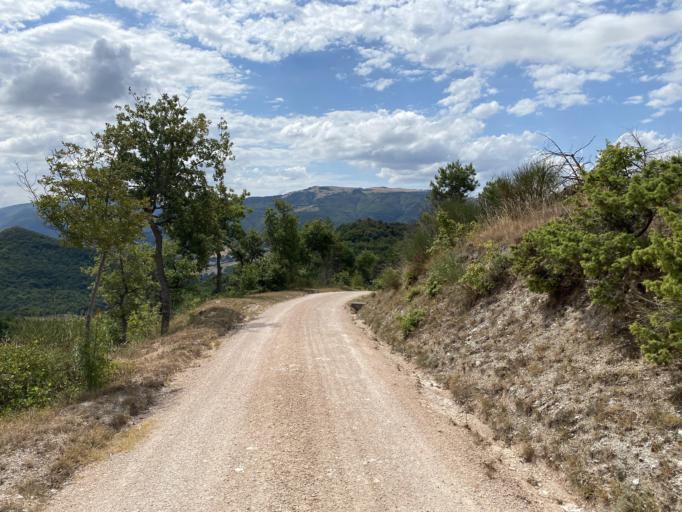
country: IT
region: The Marches
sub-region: Provincia di Pesaro e Urbino
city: Canavaccio
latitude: 43.7080
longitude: 12.7150
